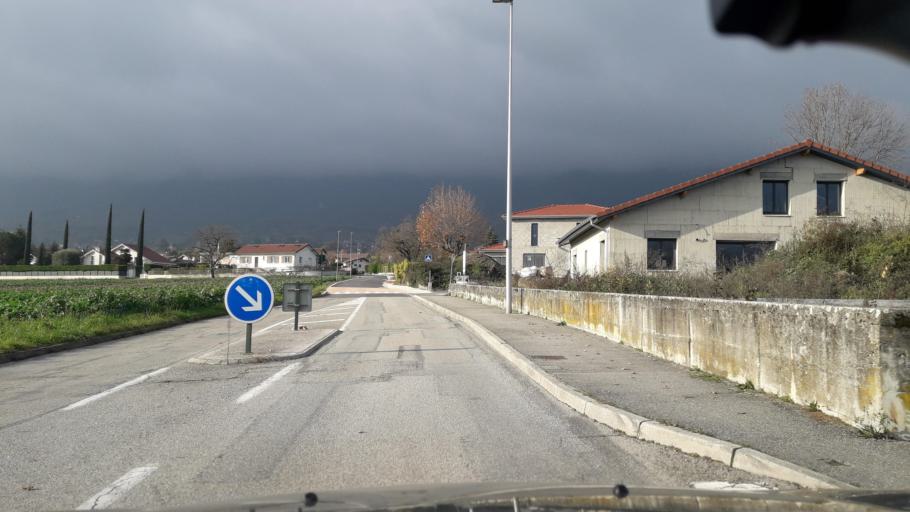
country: FR
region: Rhone-Alpes
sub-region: Departement de l'Isere
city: Saint-Nazaire-les-Eymes
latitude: 45.2443
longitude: 5.8429
